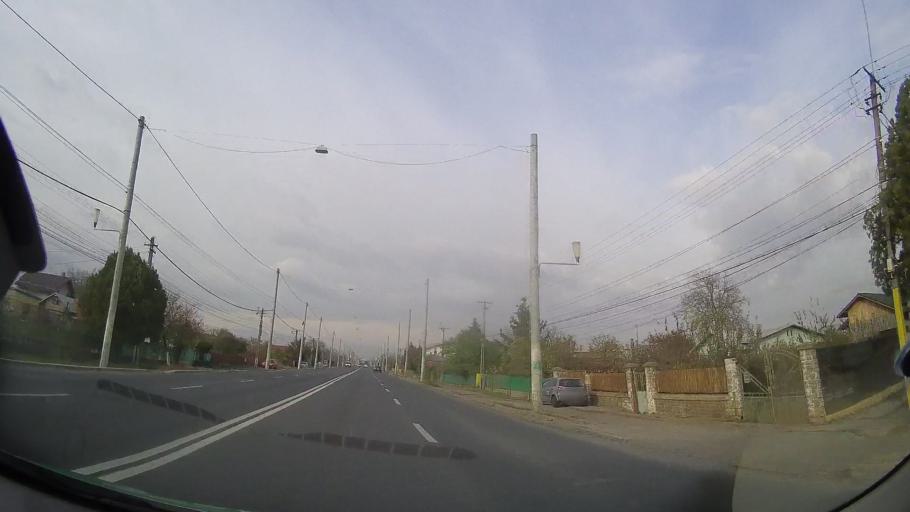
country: RO
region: Prahova
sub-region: Comuna Barcanesti
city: Tatarani
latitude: 44.8940
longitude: 26.0435
